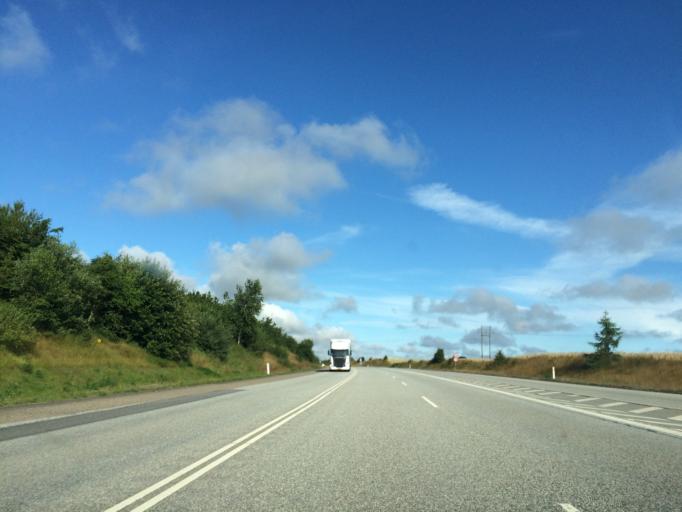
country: DK
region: Central Jutland
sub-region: Silkeborg Kommune
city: Kjellerup
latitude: 56.3572
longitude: 9.5209
